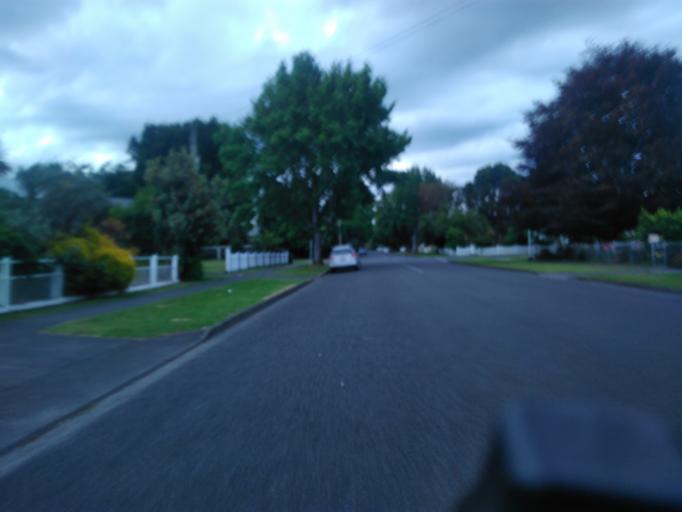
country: NZ
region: Gisborne
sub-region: Gisborne District
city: Gisborne
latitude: -38.6615
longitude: 178.0285
